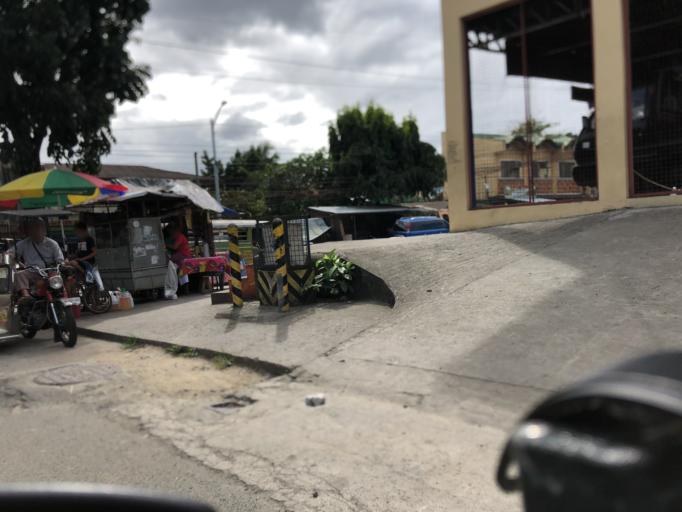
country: PH
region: Central Luzon
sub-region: Province of Bulacan
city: San Jose del Monte
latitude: 14.7572
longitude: 121.0554
